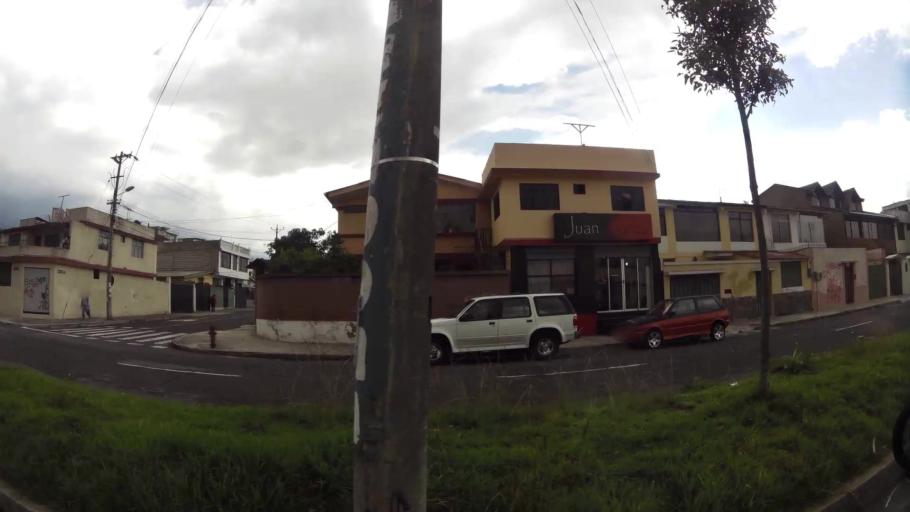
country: EC
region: Pichincha
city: Quito
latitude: -0.0882
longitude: -78.4673
